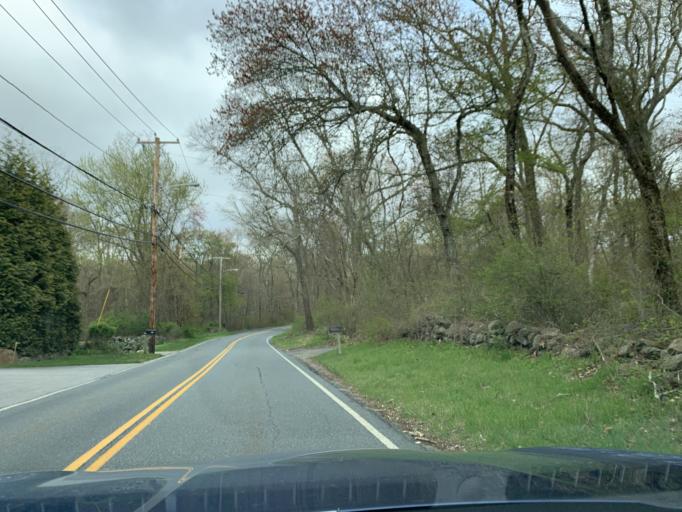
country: US
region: Rhode Island
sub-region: Washington County
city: North Kingstown
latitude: 41.5891
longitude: -71.4740
